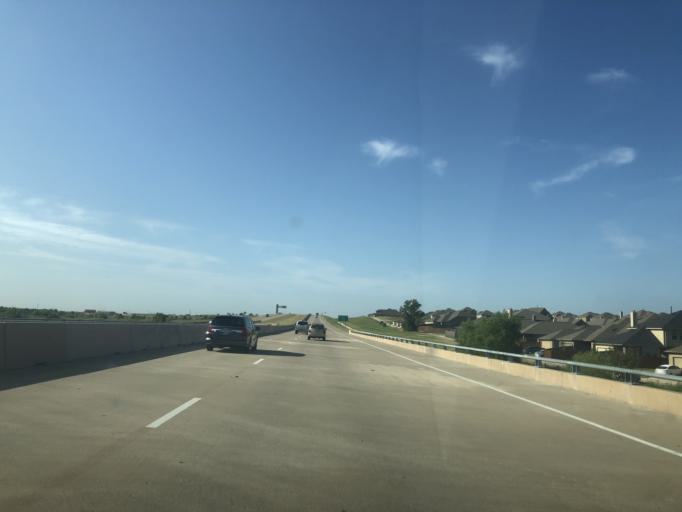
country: US
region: Texas
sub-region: Tarrant County
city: Crowley
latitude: 32.6223
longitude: -97.4127
